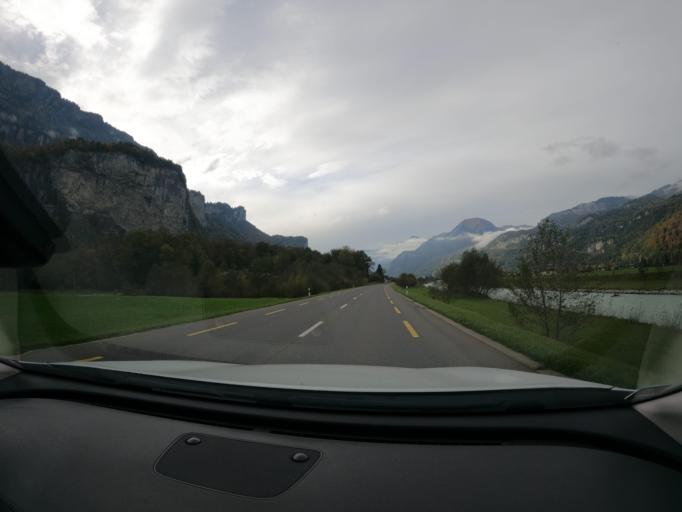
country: CH
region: Bern
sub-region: Interlaken-Oberhasli District
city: Meiringen
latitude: 46.7241
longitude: 8.1766
